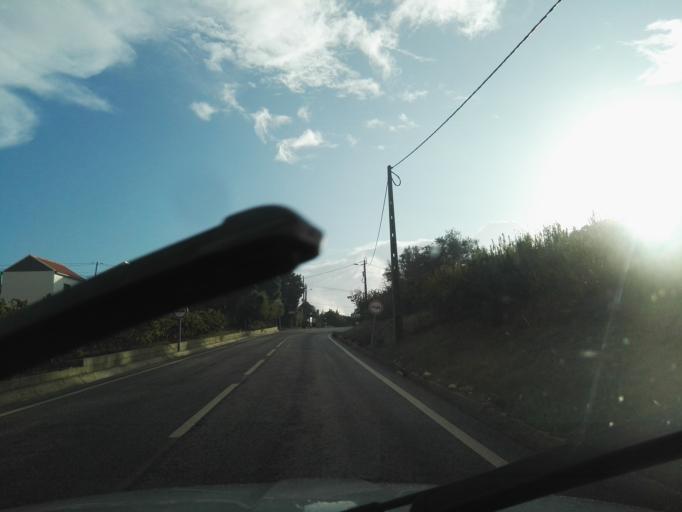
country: PT
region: Lisbon
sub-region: Arruda Dos Vinhos
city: Arruda dos Vinhos
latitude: 38.9722
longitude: -9.0491
